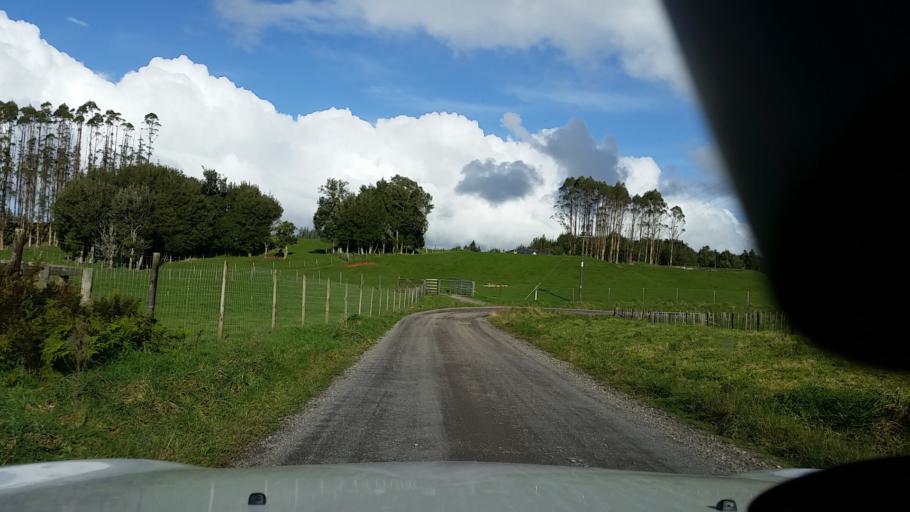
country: NZ
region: Bay of Plenty
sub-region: Rotorua District
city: Rotorua
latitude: -38.0078
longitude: 176.1983
